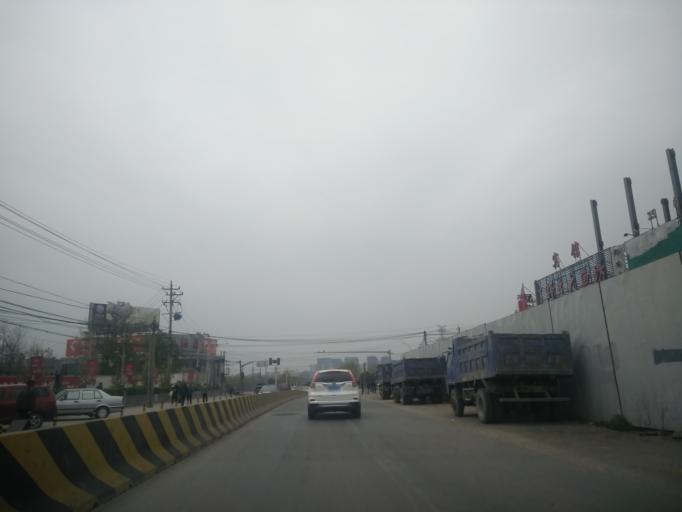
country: CN
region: Beijing
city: Jiugong
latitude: 39.8080
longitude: 116.4673
